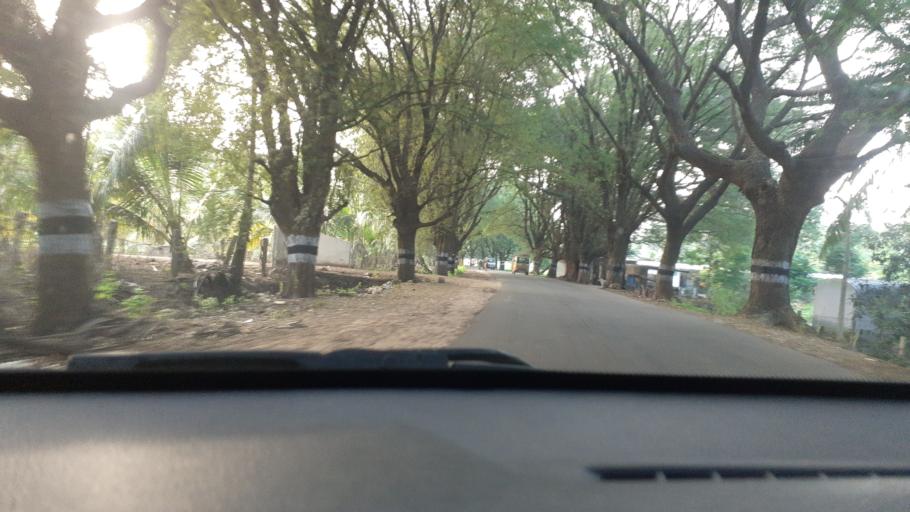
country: IN
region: Tamil Nadu
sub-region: Dindigul
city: Ayakudi
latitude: 10.4079
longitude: 77.5430
